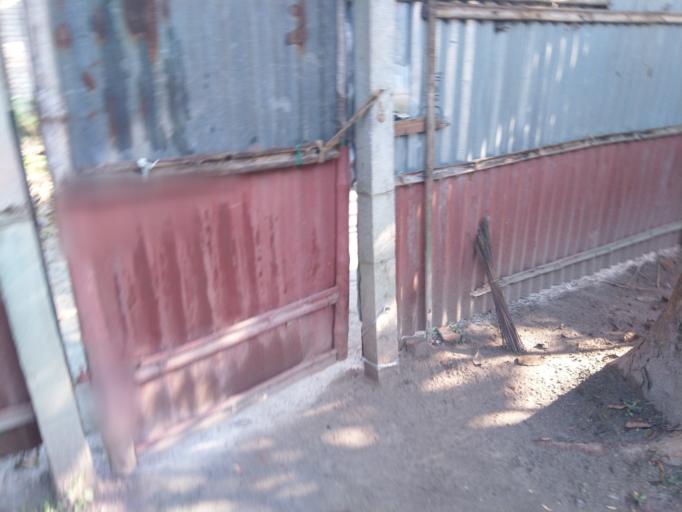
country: IN
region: West Bengal
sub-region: Uttar Dinajpur
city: Raiganj
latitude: 25.5083
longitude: 88.1437
